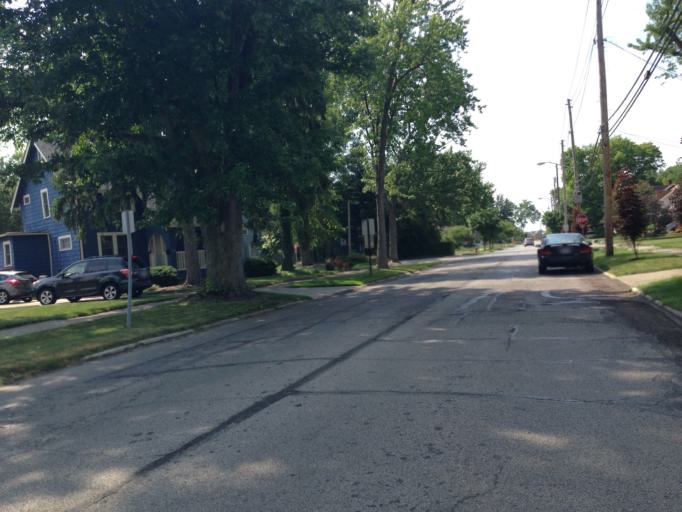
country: US
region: Ohio
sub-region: Cuyahoga County
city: Berea
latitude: 41.3679
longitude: -81.8621
